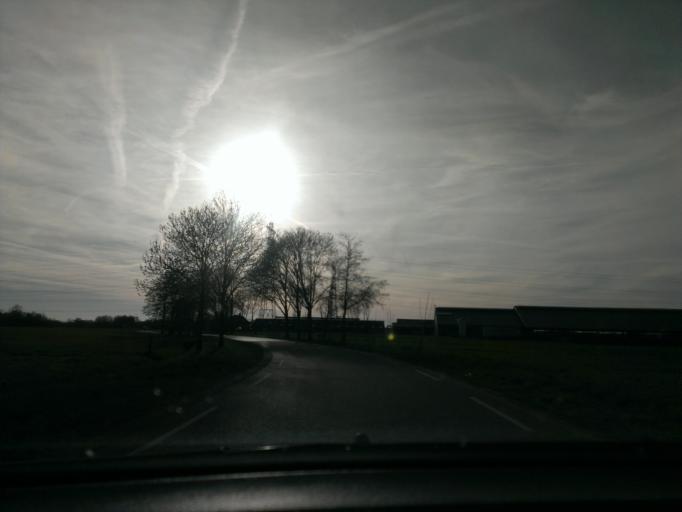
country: NL
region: Gelderland
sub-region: Gemeente Heerde
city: Heerde
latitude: 52.3950
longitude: 6.0858
